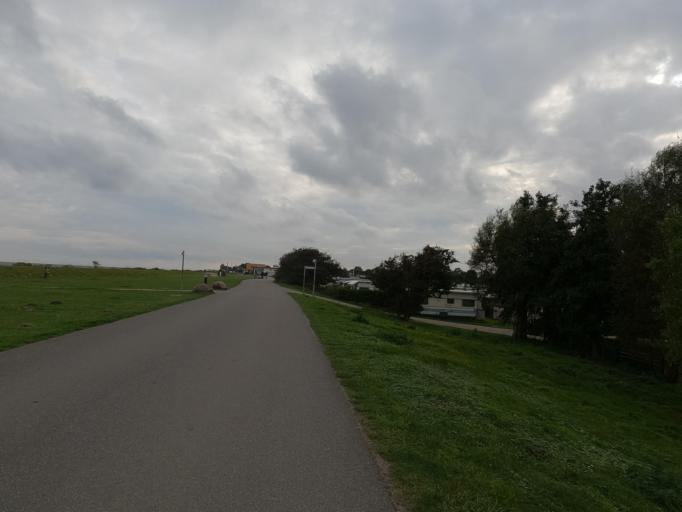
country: DE
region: Schleswig-Holstein
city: Grossenbrode
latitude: 54.3402
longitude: 11.0712
